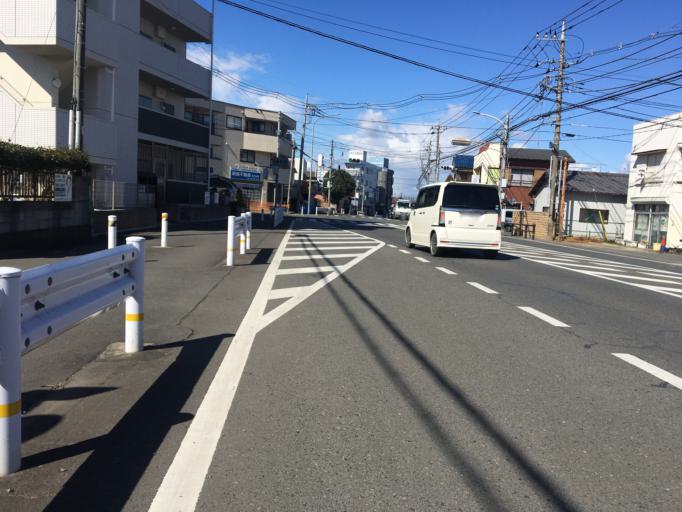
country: JP
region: Saitama
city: Shiki
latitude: 35.8068
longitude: 139.5561
